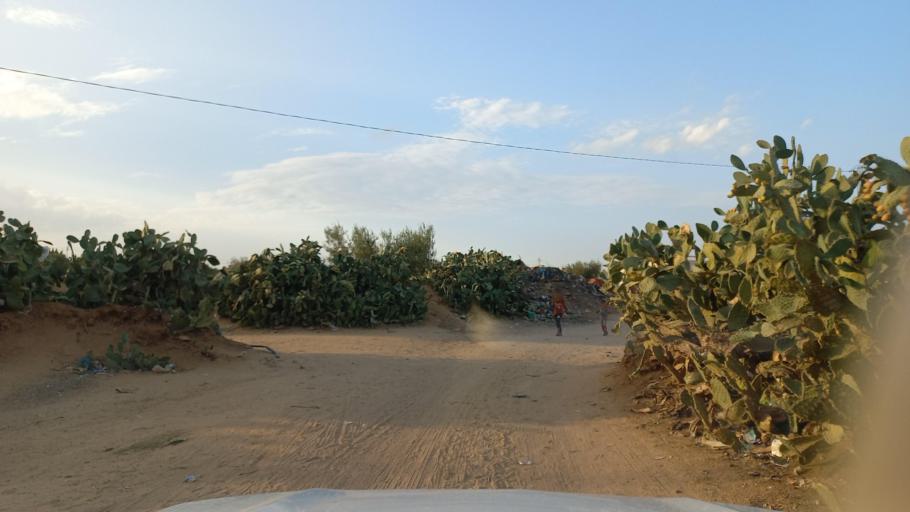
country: TN
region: Al Qasrayn
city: Kasserine
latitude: 35.2686
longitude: 9.0676
